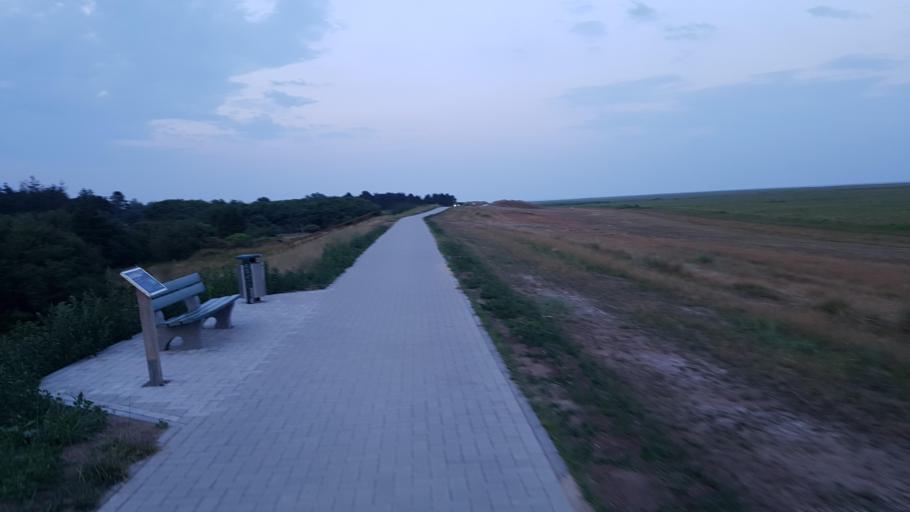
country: DE
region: Schleswig-Holstein
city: Sankt Peter-Ording
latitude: 54.2858
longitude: 8.6549
